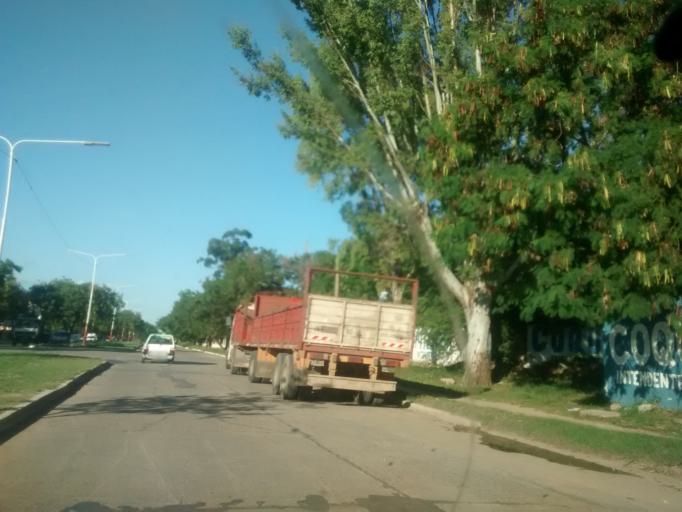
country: AR
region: Chaco
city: Resistencia
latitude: -27.4543
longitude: -59.0185
